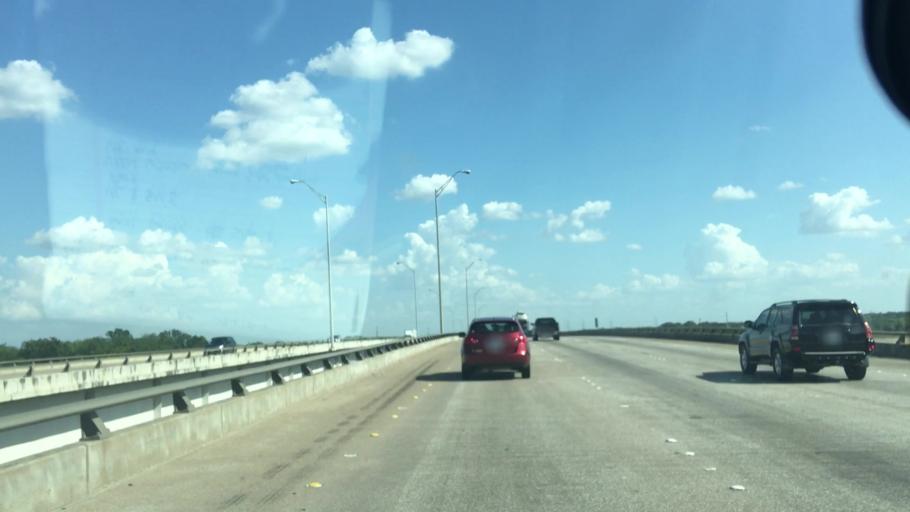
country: US
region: Texas
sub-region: Dallas County
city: Dallas
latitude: 32.7383
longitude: -96.7665
